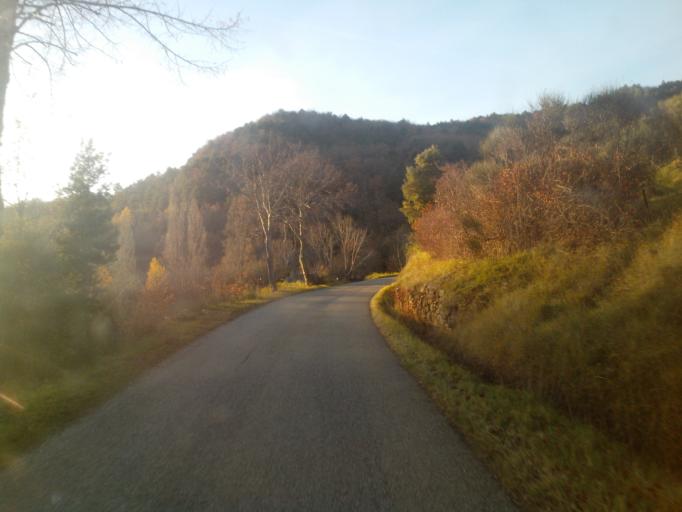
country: FR
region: Languedoc-Roussillon
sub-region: Departement de l'Aude
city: Quillan
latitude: 42.9365
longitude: 2.1155
